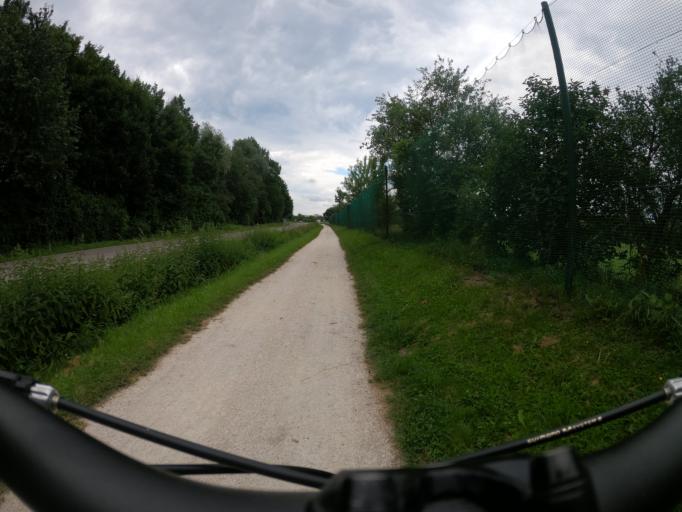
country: DE
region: Bavaria
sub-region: Swabia
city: Neu-Ulm
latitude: 48.4127
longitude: 10.0221
